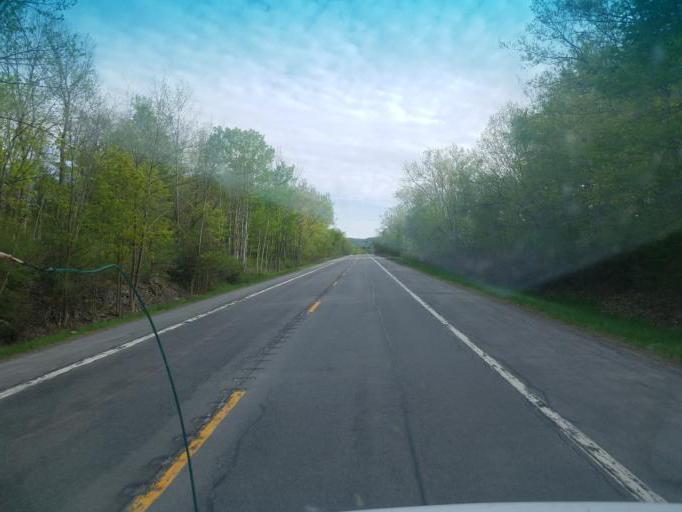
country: US
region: New York
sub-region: Herkimer County
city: Little Falls
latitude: 43.0213
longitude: -74.8778
